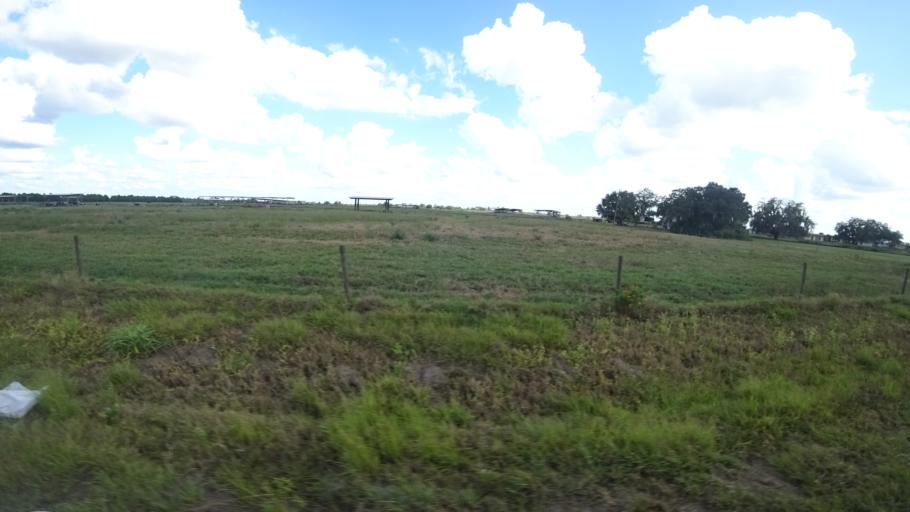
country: US
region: Florida
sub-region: DeSoto County
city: Nocatee
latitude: 27.2926
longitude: -82.1134
